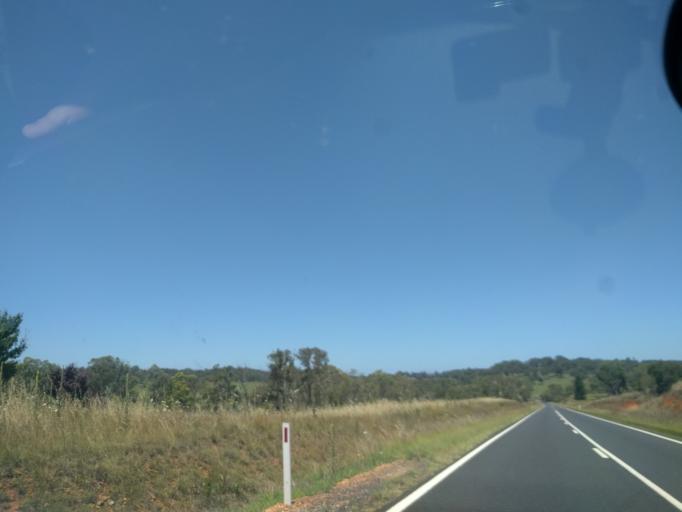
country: AU
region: New South Wales
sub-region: Armidale Dumaresq
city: Armidale
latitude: -30.5340
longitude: 151.7240
